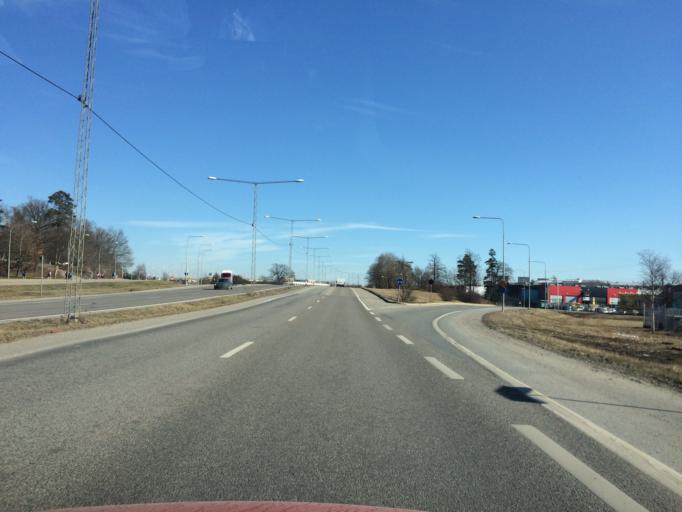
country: SE
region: Stockholm
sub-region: Huddinge Kommun
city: Segeltorp
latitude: 59.2879
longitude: 17.9398
